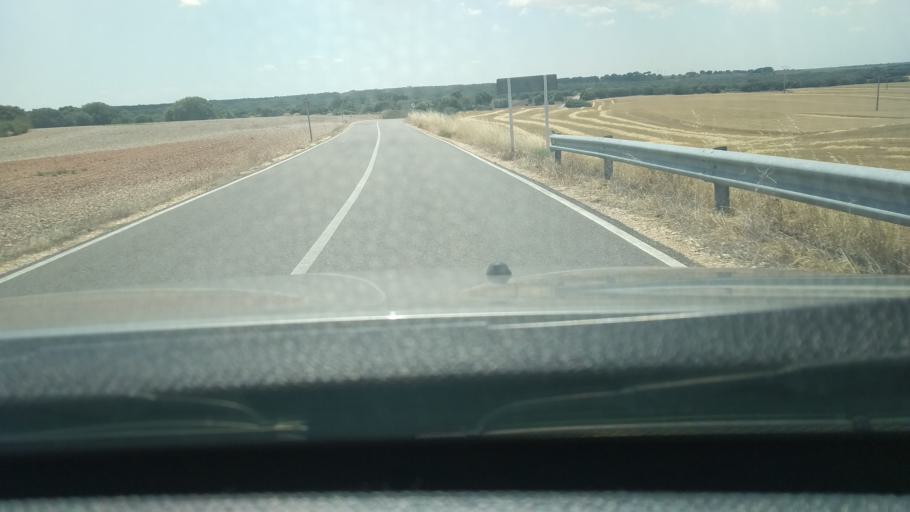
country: ES
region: Castille and Leon
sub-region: Provincia de Burgos
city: Avellanosa de Muno
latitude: 41.9744
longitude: -3.8091
